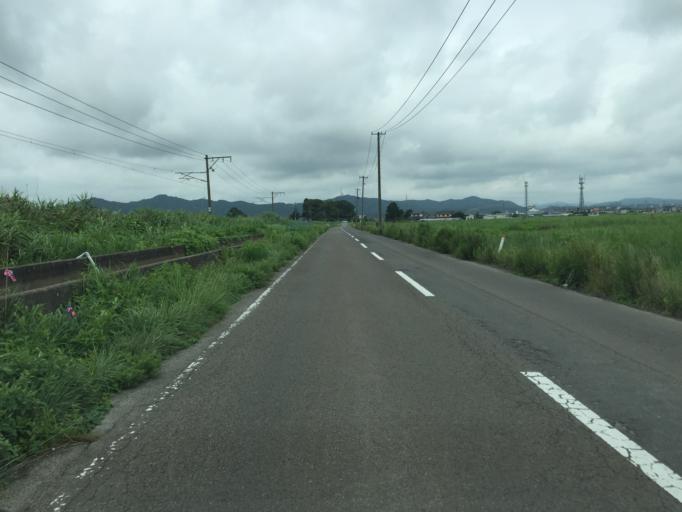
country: JP
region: Miyagi
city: Watari
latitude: 38.0281
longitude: 140.8720
